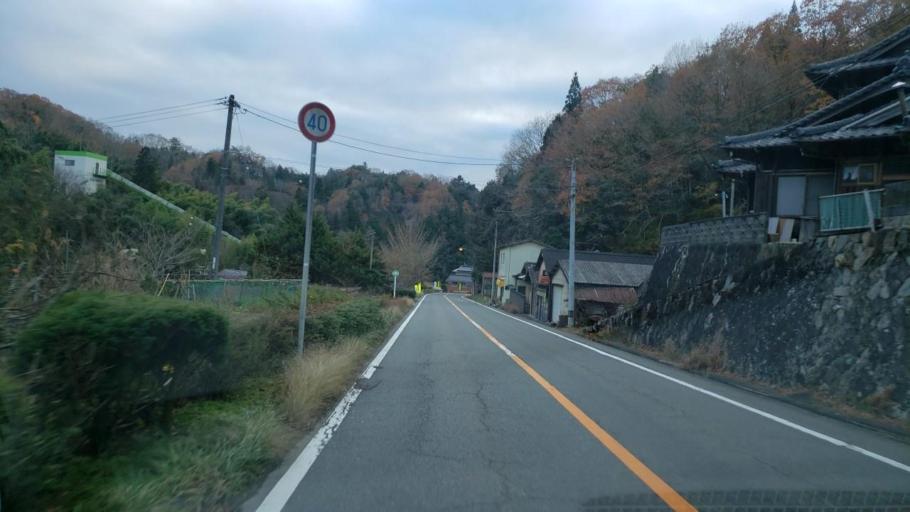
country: JP
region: Tokushima
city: Wakimachi
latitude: 34.1915
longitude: 134.1752
